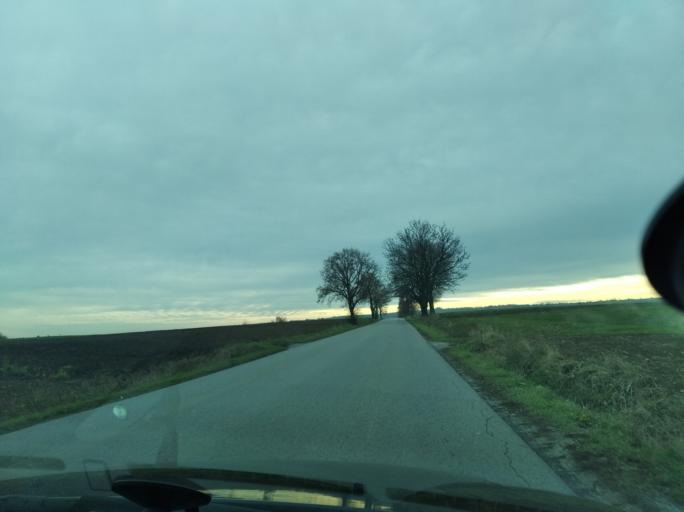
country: PL
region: Subcarpathian Voivodeship
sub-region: Powiat lancucki
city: Wysoka
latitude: 50.0233
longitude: 22.2593
